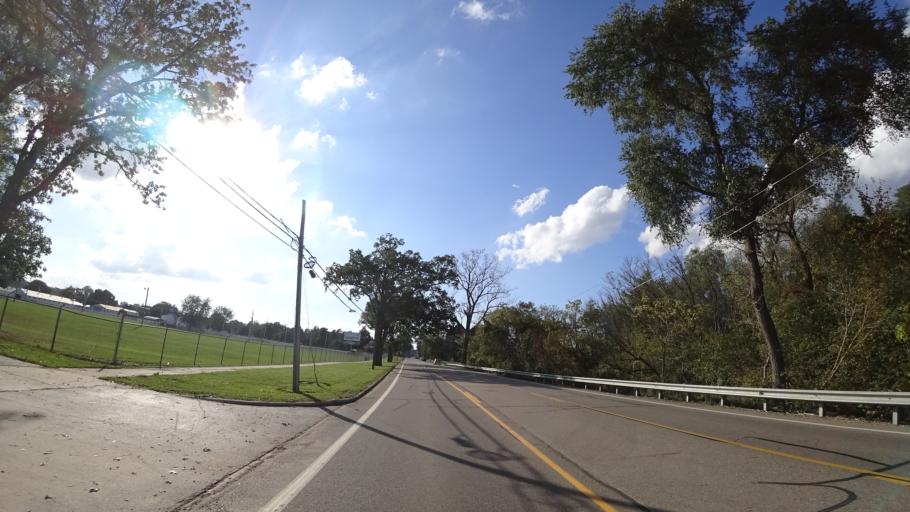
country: US
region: Michigan
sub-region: Saint Joseph County
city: Centreville
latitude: 41.9237
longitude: -85.5169
